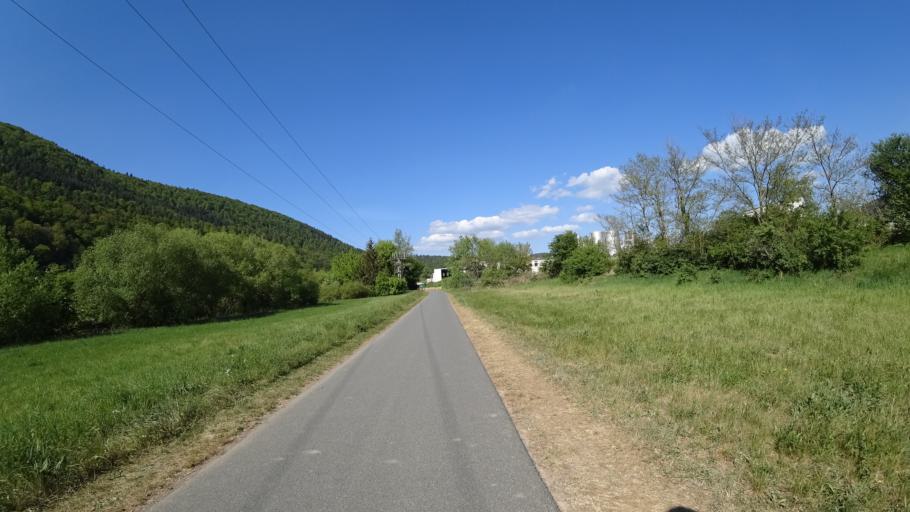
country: DE
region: Bavaria
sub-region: Regierungsbezirk Unterfranken
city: Burgstadt
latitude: 49.7323
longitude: 9.2723
